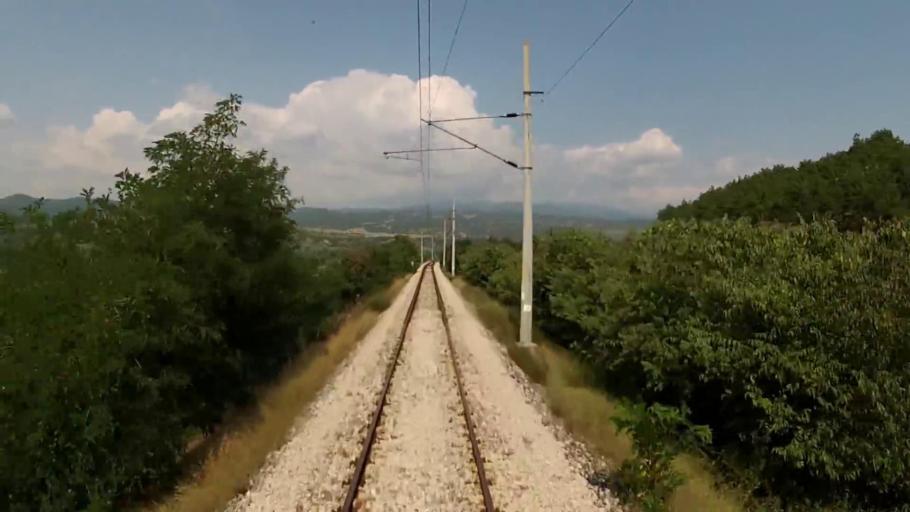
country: BG
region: Blagoevgrad
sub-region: Obshtina Strumyani
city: Strumyani
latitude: 41.6438
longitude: 23.1979
